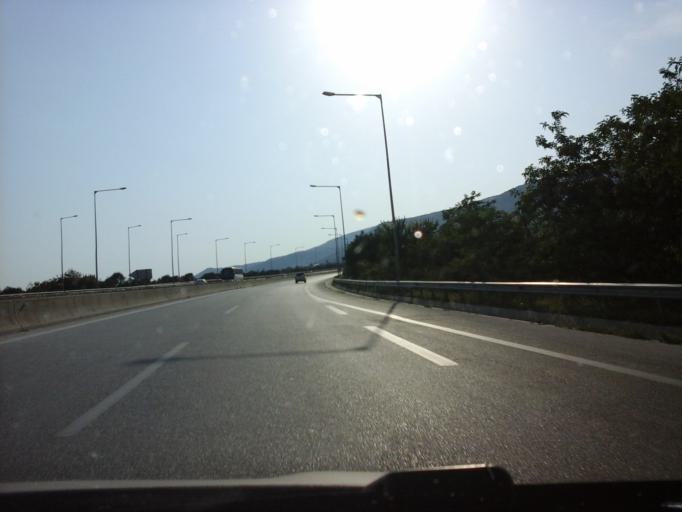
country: GR
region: East Macedonia and Thrace
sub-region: Nomos Kavalas
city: Chrysoupolis
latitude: 40.9893
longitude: 24.6317
